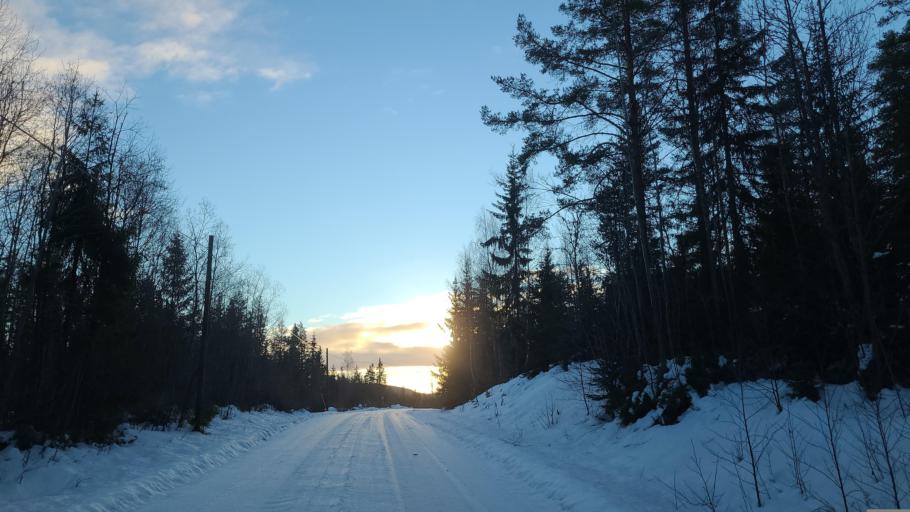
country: SE
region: Gaevleborg
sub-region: Bollnas Kommun
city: Kilafors
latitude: 61.3752
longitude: 16.6816
